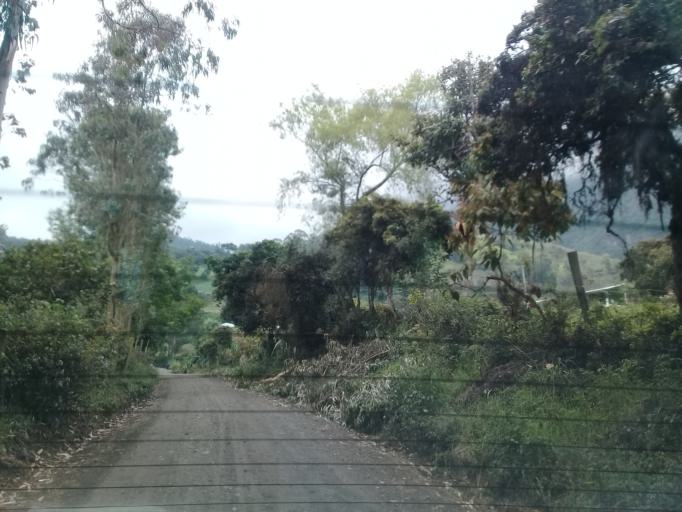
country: CO
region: Cundinamarca
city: Une
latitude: 4.4016
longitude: -73.9894
